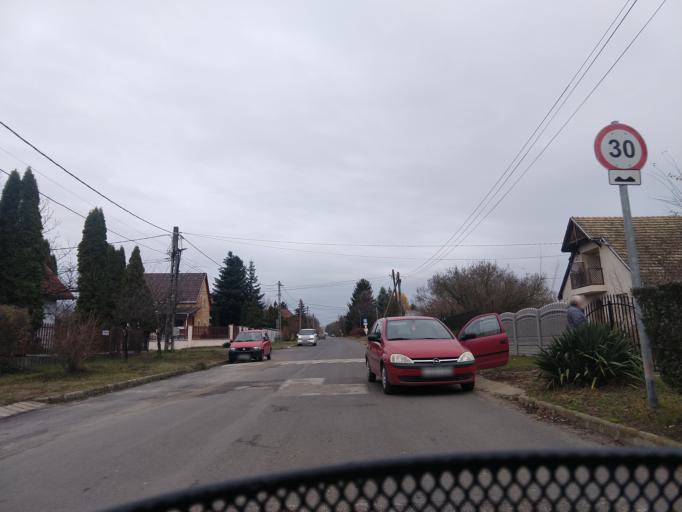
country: HU
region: Pest
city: Erdokertes
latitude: 47.6678
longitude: 19.2927
